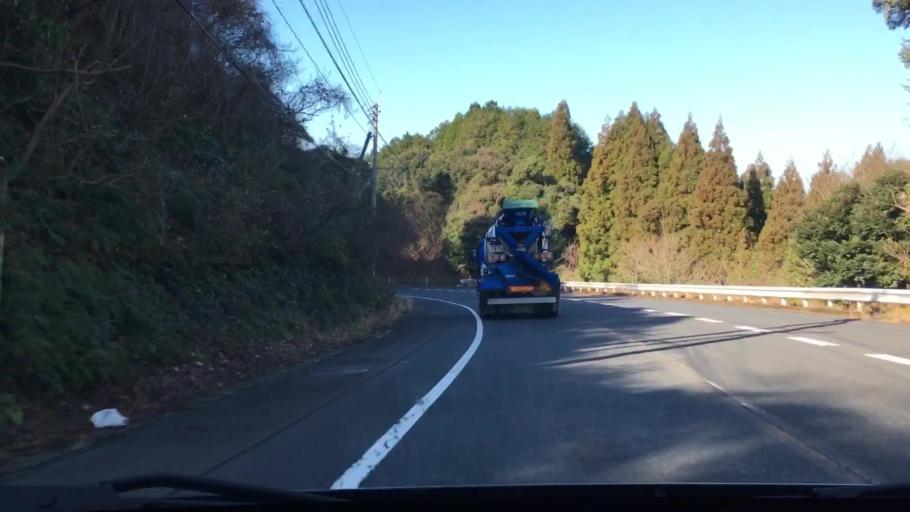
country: JP
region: Kagoshima
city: Kajiki
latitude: 31.7644
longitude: 130.6858
